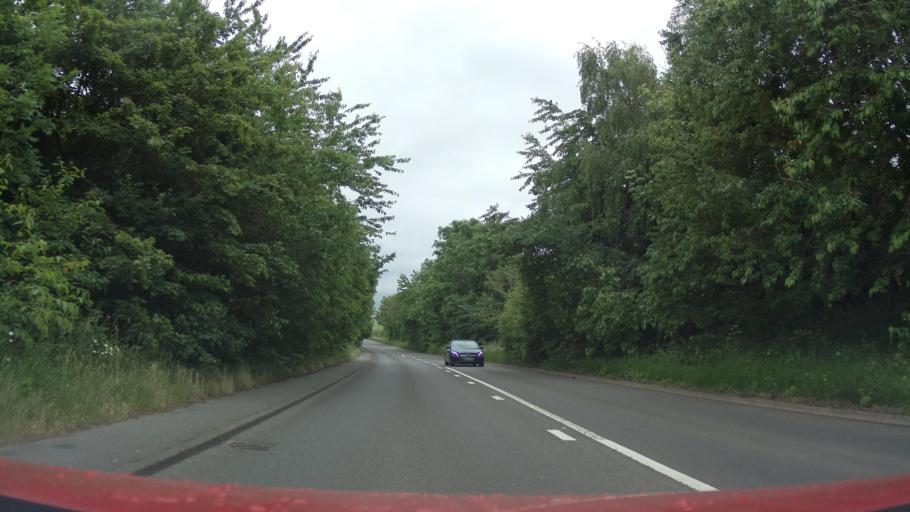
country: GB
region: England
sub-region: Staffordshire
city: Burton upon Trent
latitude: 52.8500
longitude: -1.6796
